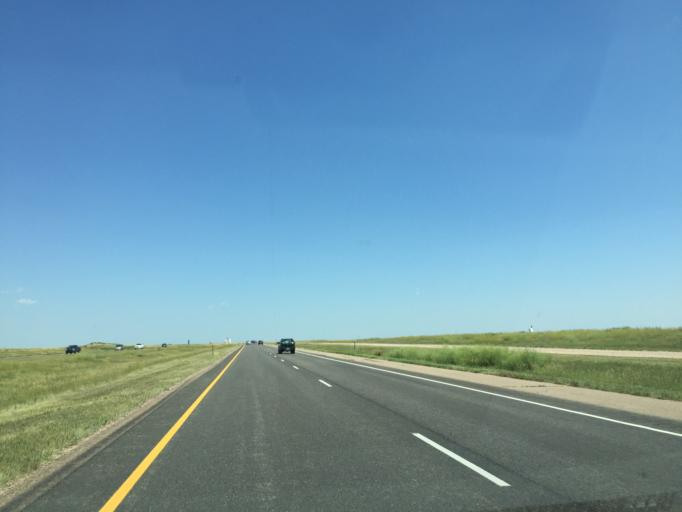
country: US
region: Colorado
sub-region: Lincoln County
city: Hugo
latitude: 39.2816
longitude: -103.3231
